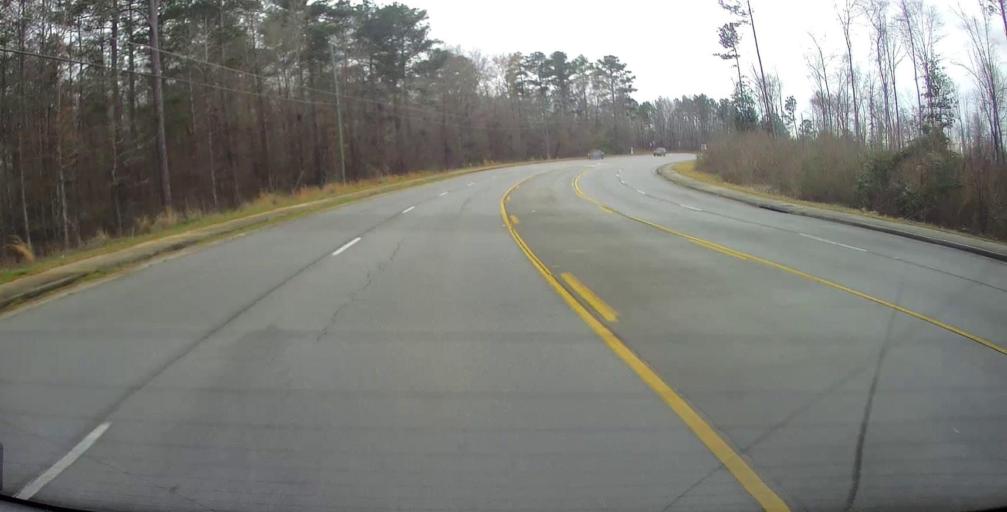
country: US
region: Georgia
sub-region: Bibb County
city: Macon
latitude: 32.8993
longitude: -83.7078
